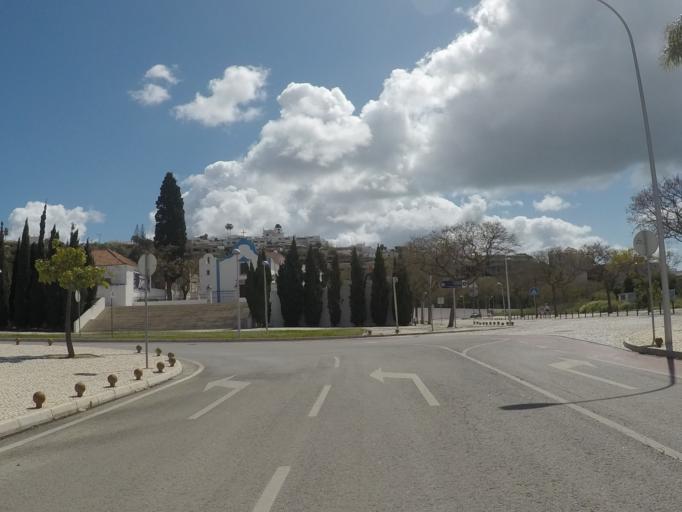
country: PT
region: Faro
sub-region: Albufeira
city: Albufeira
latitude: 37.0854
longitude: -8.2653
